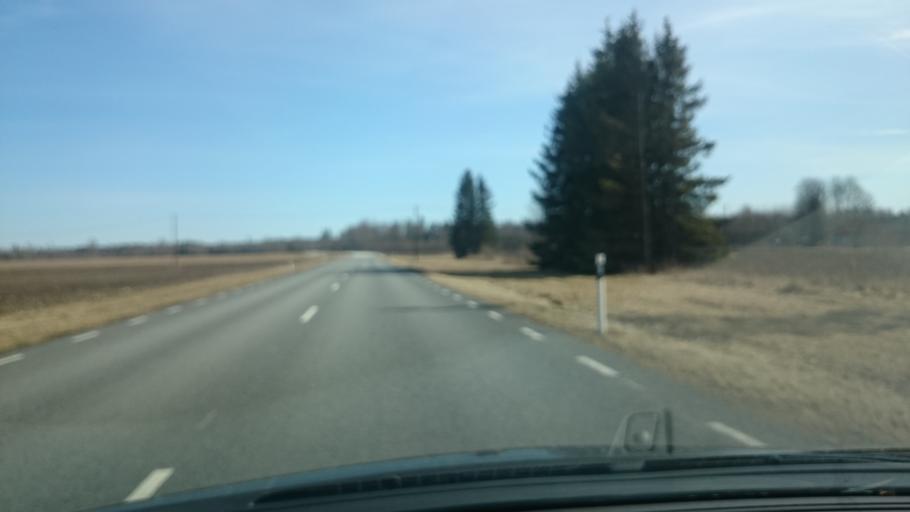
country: EE
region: Paernumaa
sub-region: Tootsi vald
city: Tootsi
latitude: 58.6654
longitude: 24.7888
